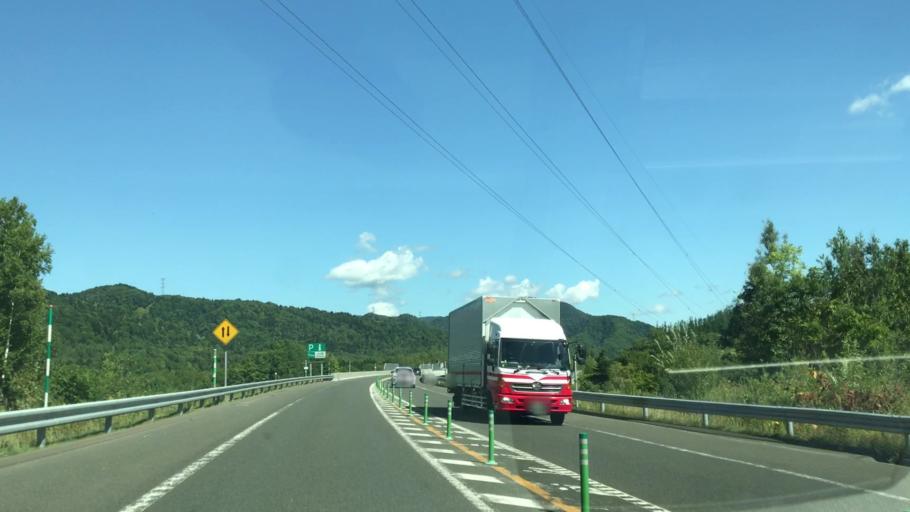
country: JP
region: Hokkaido
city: Shimo-furano
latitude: 43.0011
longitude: 142.4110
